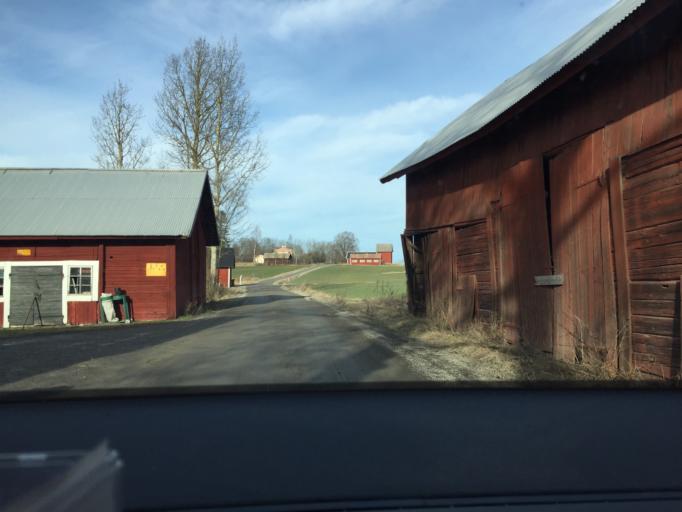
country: SE
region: OErebro
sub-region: Hallsbergs Kommun
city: Skollersta
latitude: 59.1379
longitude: 15.4168
